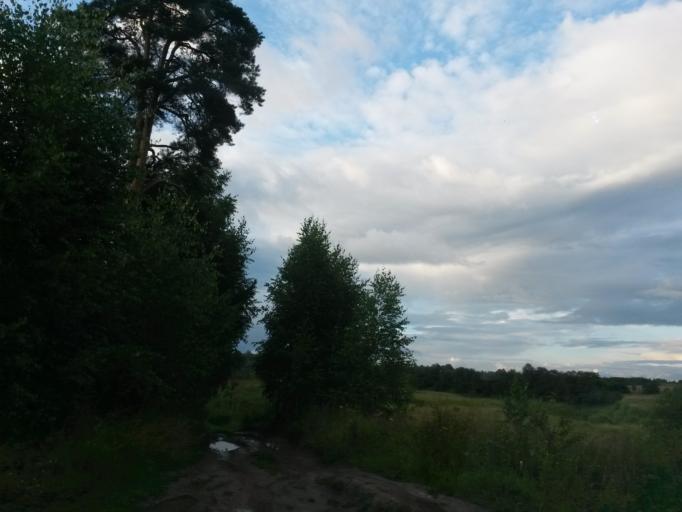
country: RU
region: Jaroslavl
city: Tutayev
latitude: 57.9340
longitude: 39.4471
